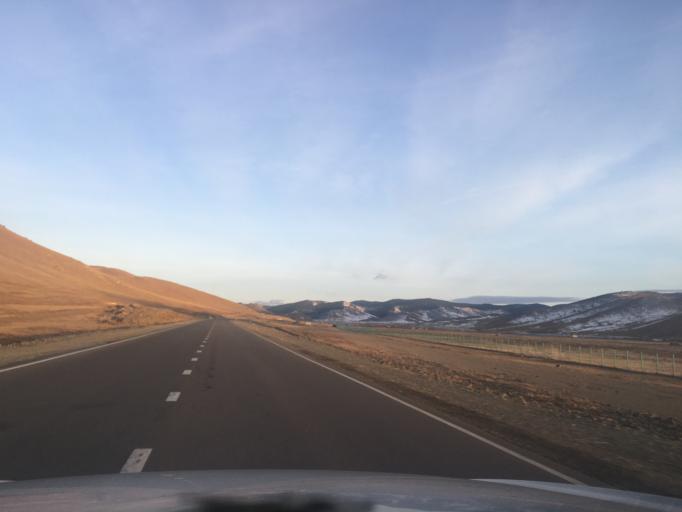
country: MN
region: Central Aimak
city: Mandal
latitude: 48.1148
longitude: 106.6993
